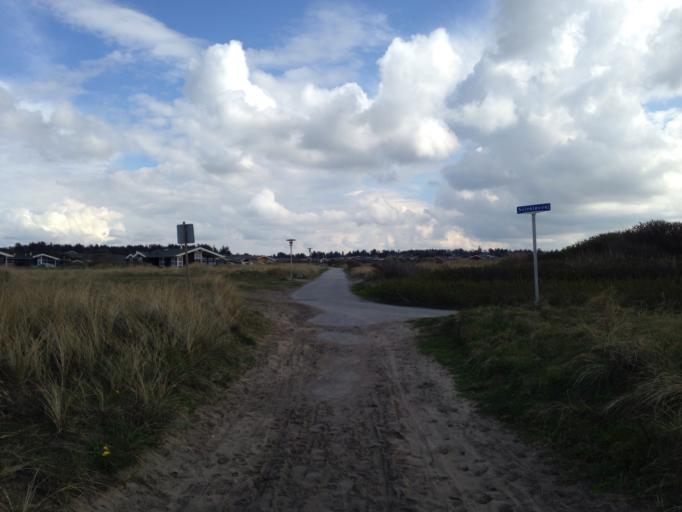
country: DK
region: North Denmark
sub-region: Hjorring Kommune
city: Hjorring
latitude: 57.4930
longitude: 9.8284
